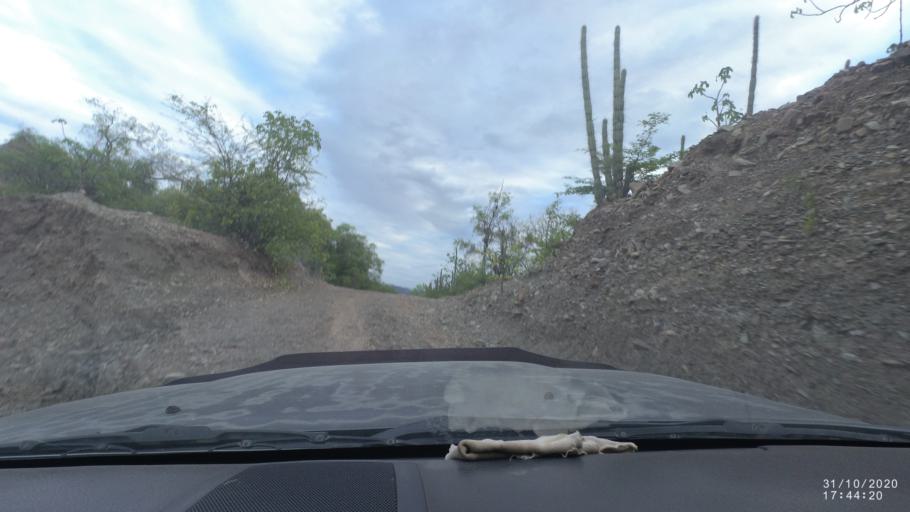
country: BO
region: Chuquisaca
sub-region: Provincia Zudanez
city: Mojocoya
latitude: -18.6103
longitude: -64.5475
